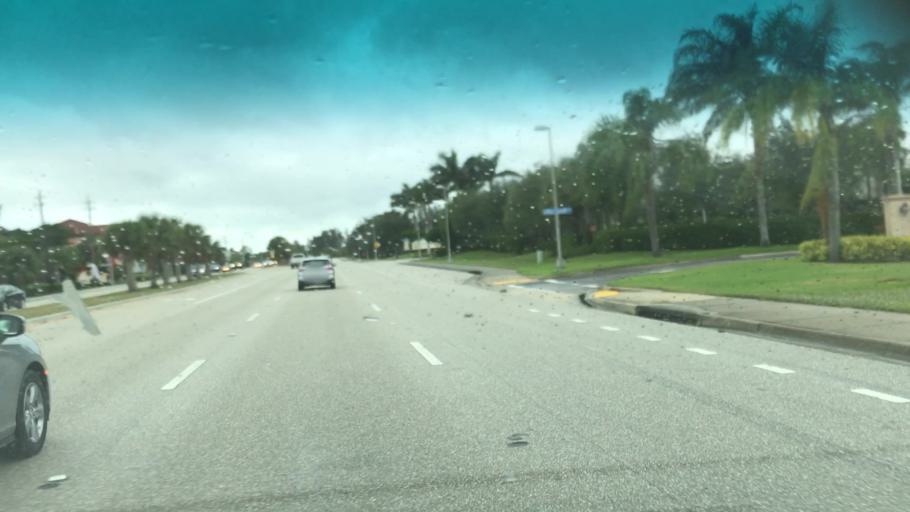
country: US
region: Florida
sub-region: Lee County
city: Harlem Heights
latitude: 26.5204
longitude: -81.9143
